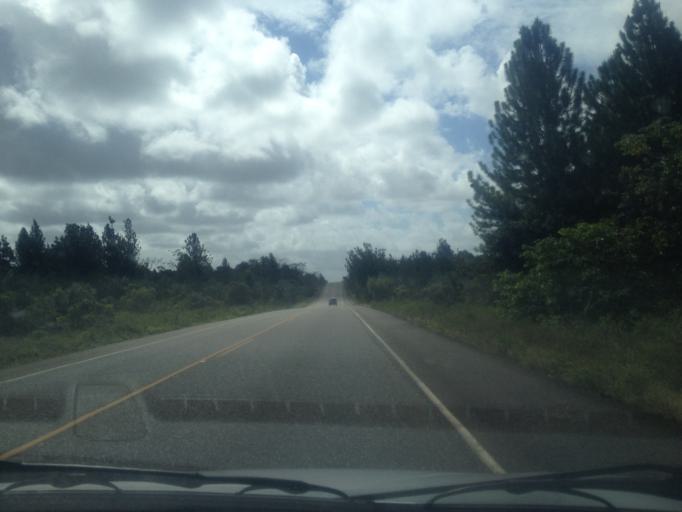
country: BR
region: Bahia
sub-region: Entre Rios
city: Entre Rios
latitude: -12.2753
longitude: -37.8802
